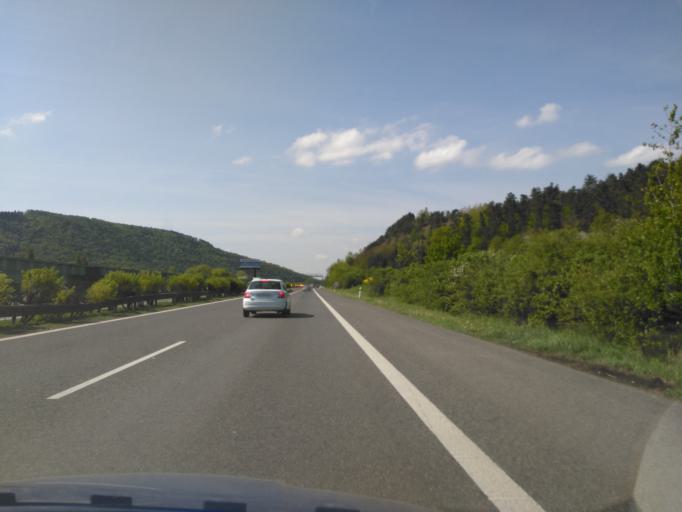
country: CZ
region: Central Bohemia
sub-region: Okres Beroun
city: Kraluv Dvur
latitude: 49.9311
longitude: 14.0164
